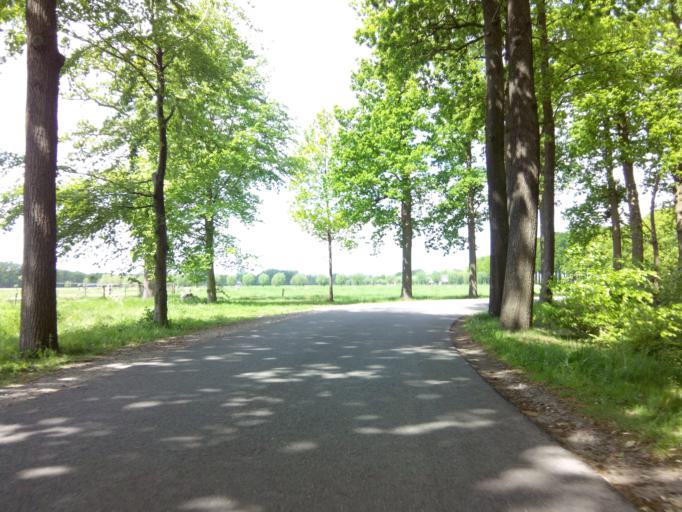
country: NL
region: Utrecht
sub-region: Gemeente Utrechtse Heuvelrug
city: Overberg
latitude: 52.0695
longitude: 5.4732
